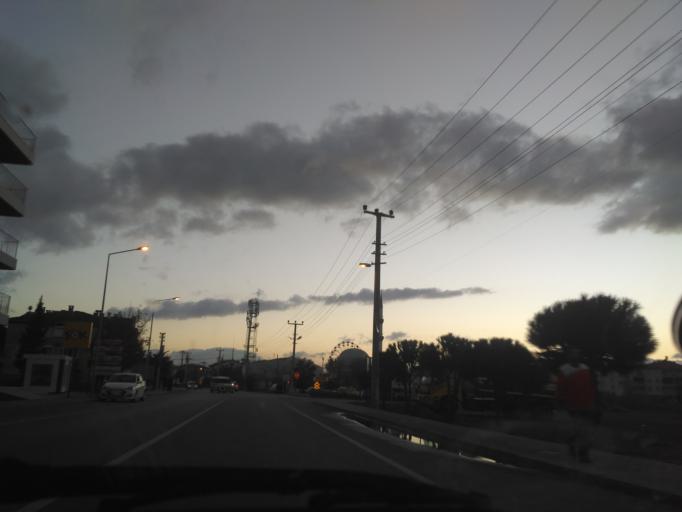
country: TR
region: Balikesir
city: Ayvalik
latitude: 39.2741
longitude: 26.6682
